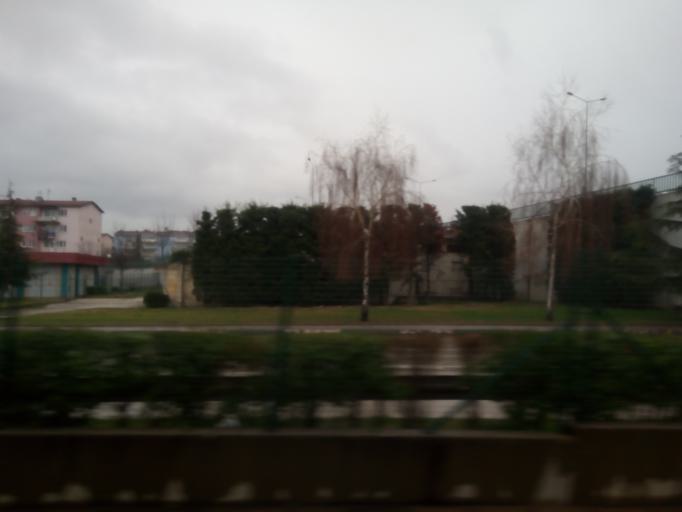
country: TR
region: Bursa
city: Niluefer
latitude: 40.2392
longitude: 28.9729
